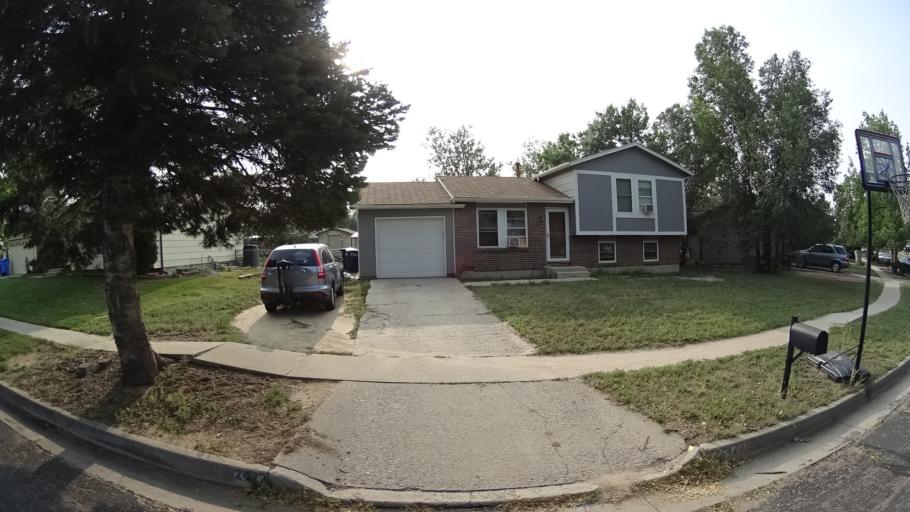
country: US
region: Colorado
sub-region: El Paso County
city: Stratmoor
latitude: 38.7977
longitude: -104.7522
